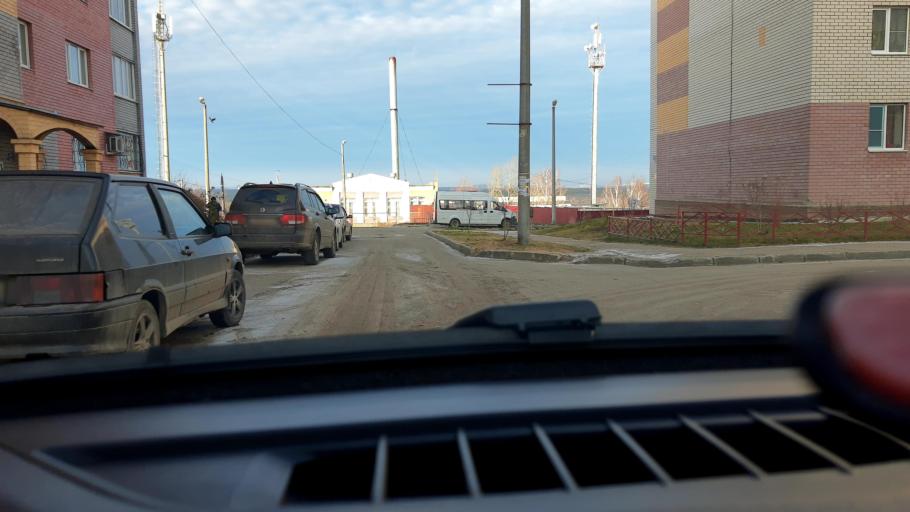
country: RU
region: Nizjnij Novgorod
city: Kstovo
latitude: 56.1470
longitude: 44.1770
